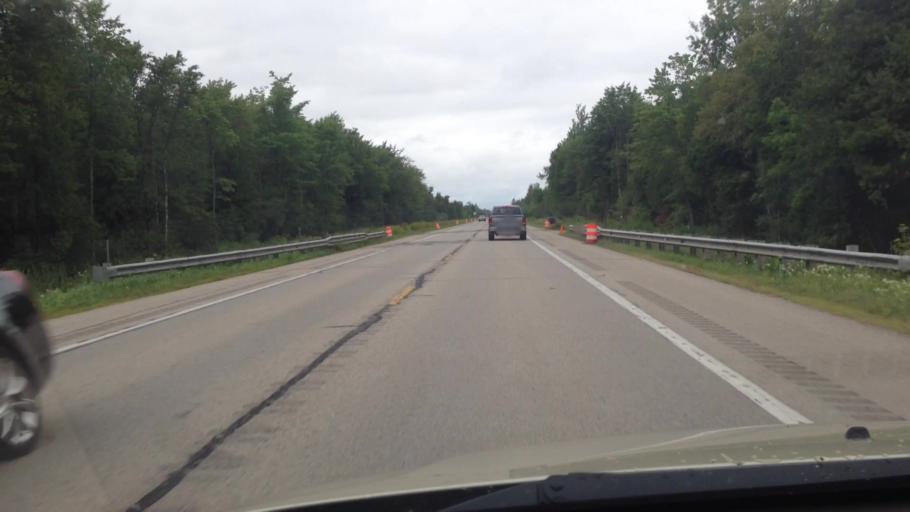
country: US
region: Michigan
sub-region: Delta County
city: Escanaba
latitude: 45.6042
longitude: -87.2227
